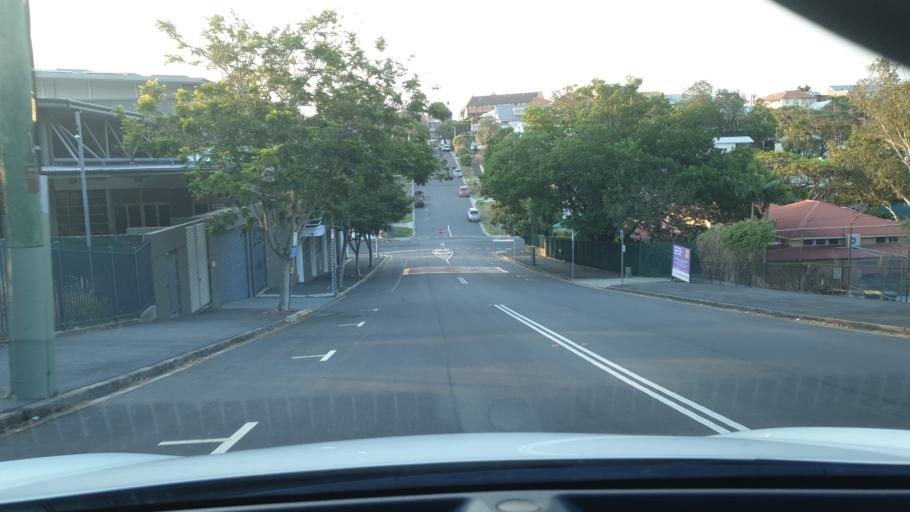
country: AU
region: Queensland
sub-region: Brisbane
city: Fortitude Valley
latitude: -27.4580
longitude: 153.0280
